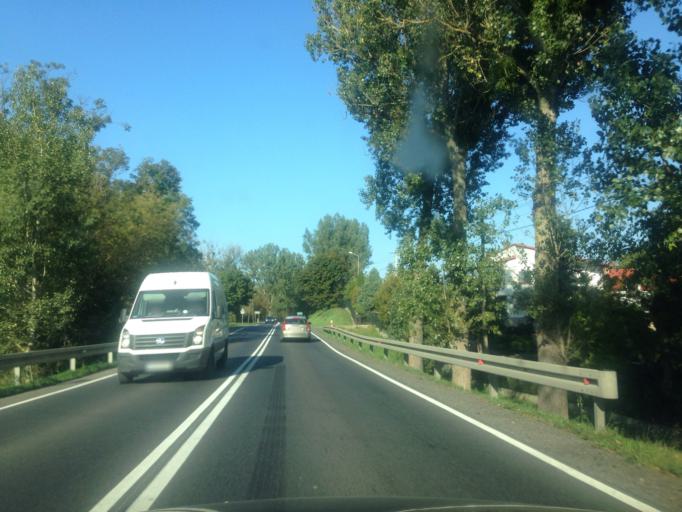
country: PL
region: Kujawsko-Pomorskie
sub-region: Powiat brodnicki
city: Bobrowo
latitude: 53.2451
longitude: 19.3005
